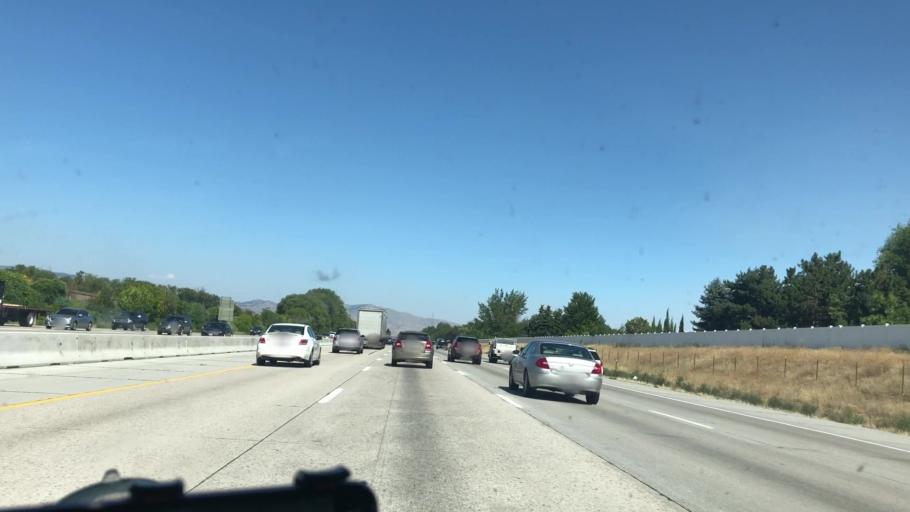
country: US
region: Idaho
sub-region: Ada County
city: Meridian
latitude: 43.5972
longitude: -116.3289
